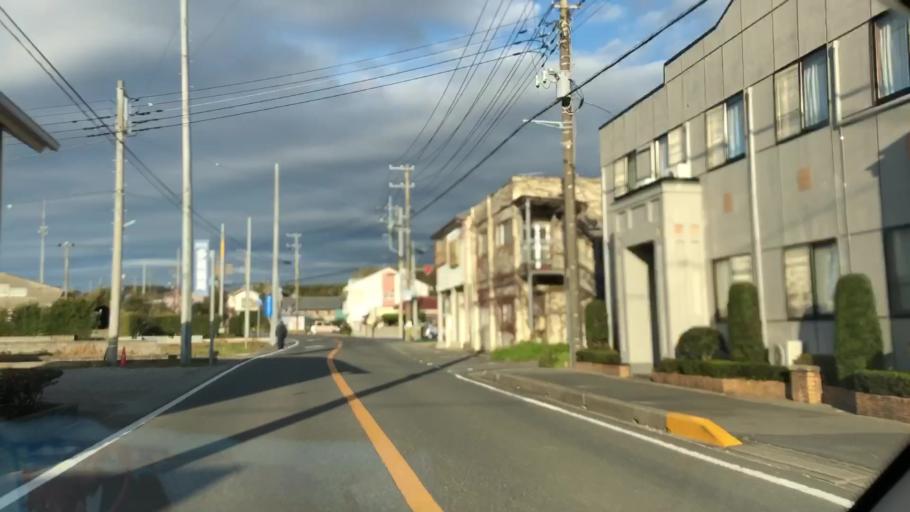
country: JP
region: Chiba
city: Tateyama
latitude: 34.9753
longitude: 139.9580
